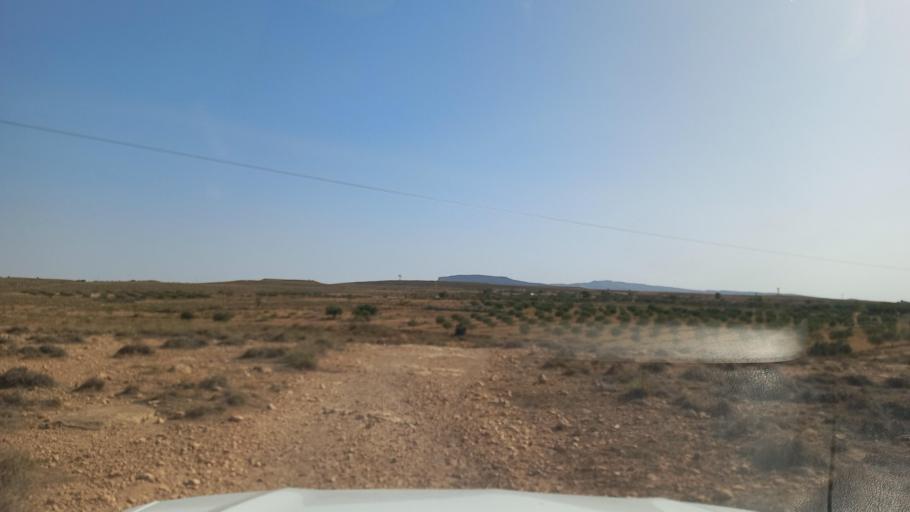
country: TN
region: Al Qasrayn
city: Kasserine
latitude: 35.2065
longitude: 8.9727
